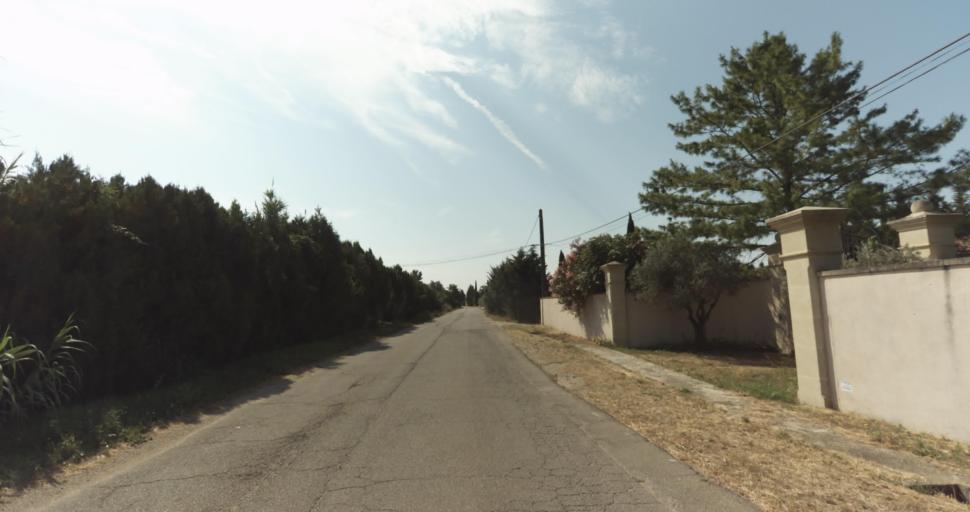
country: FR
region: Provence-Alpes-Cote d'Azur
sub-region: Departement du Vaucluse
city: Carpentras
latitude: 44.0249
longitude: 5.0333
